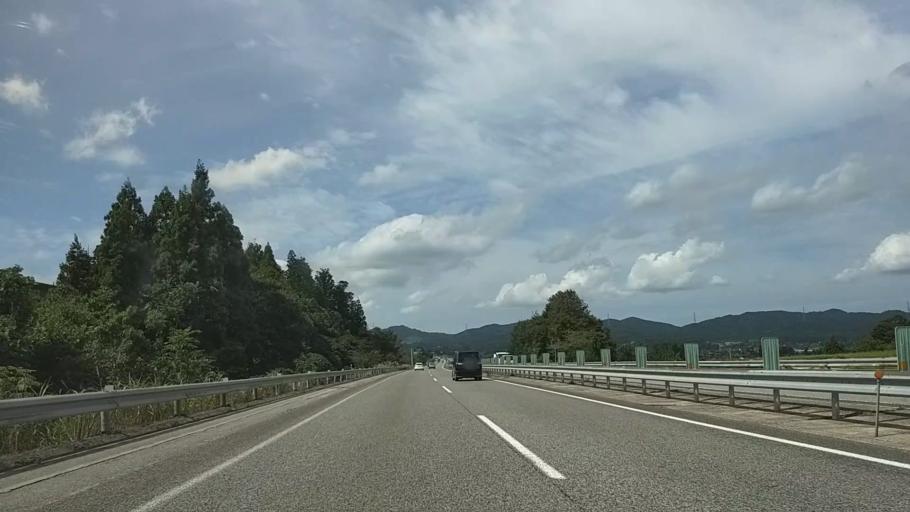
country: JP
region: Toyama
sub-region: Oyabe Shi
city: Oyabe
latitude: 36.6272
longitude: 136.8658
